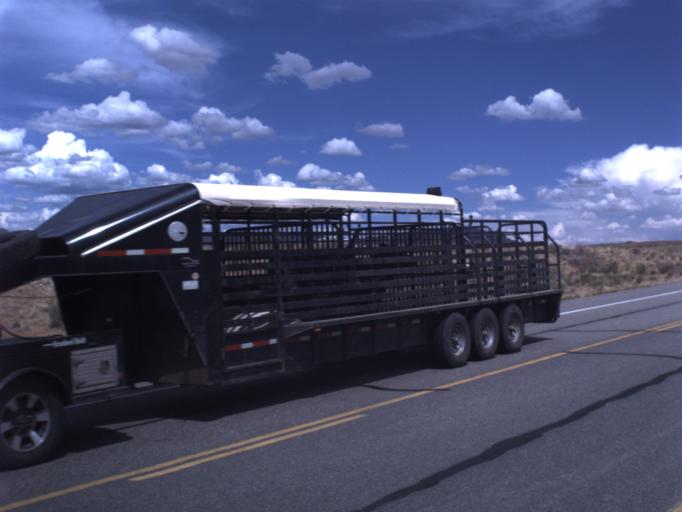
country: US
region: Utah
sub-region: Carbon County
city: East Carbon City
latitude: 38.9918
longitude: -110.1355
